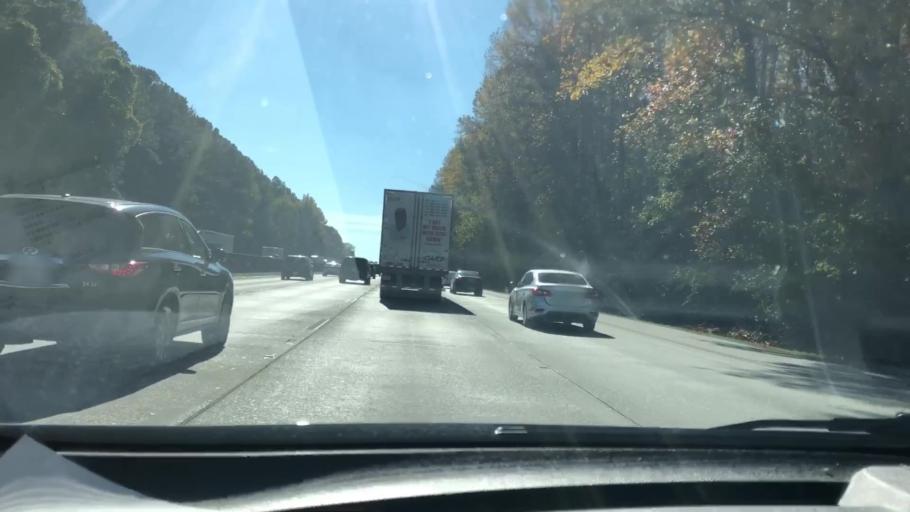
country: US
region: Georgia
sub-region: DeKalb County
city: Tucker
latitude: 33.8661
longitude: -84.2492
